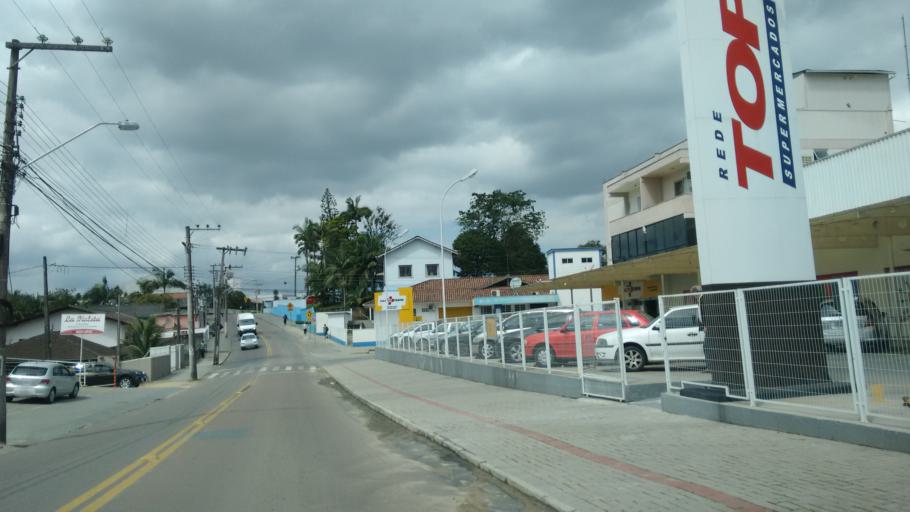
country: BR
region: Santa Catarina
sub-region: Blumenau
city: Blumenau
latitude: -26.8655
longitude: -49.1218
